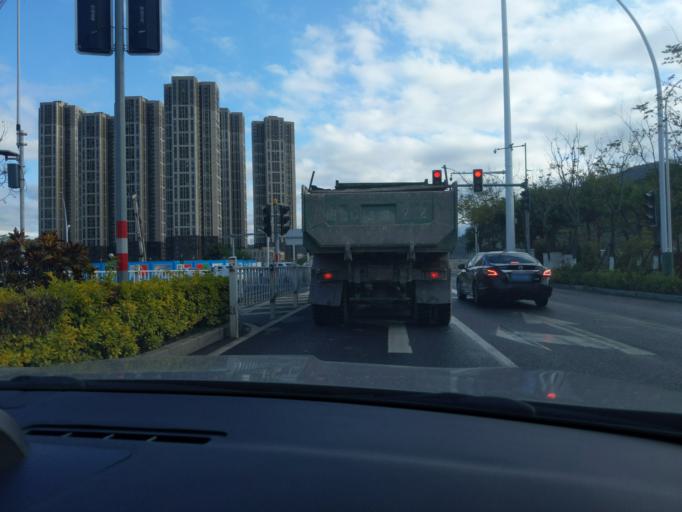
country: CN
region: Fujian
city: Houxi
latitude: 24.6350
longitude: 118.0729
